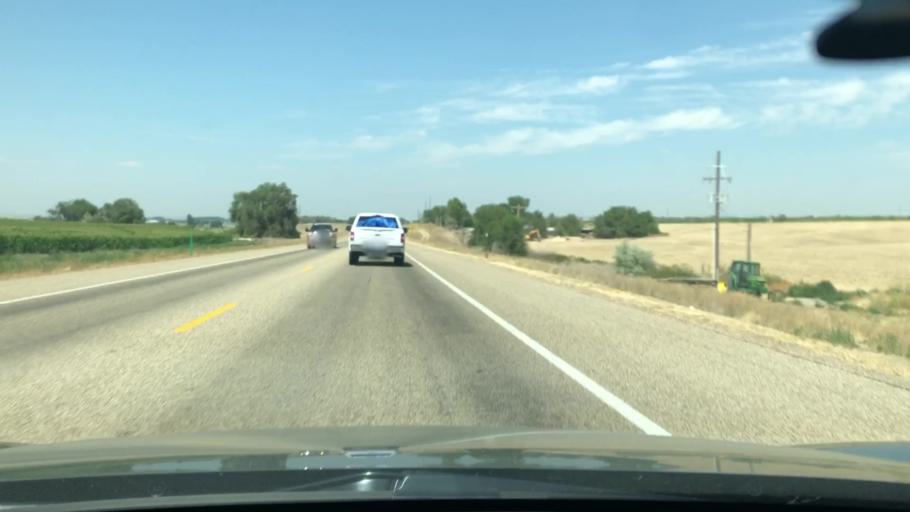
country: US
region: Oregon
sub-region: Malheur County
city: Nyssa
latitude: 43.8397
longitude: -116.9544
